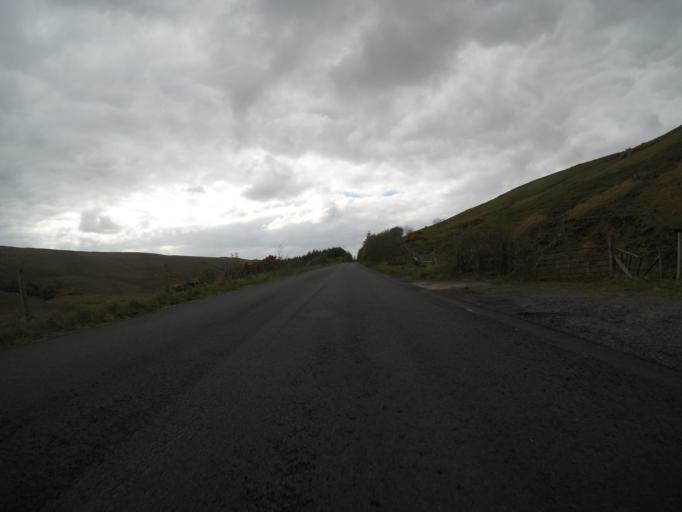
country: GB
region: Scotland
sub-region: Highland
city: Isle of Skye
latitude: 57.2970
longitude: -6.2815
